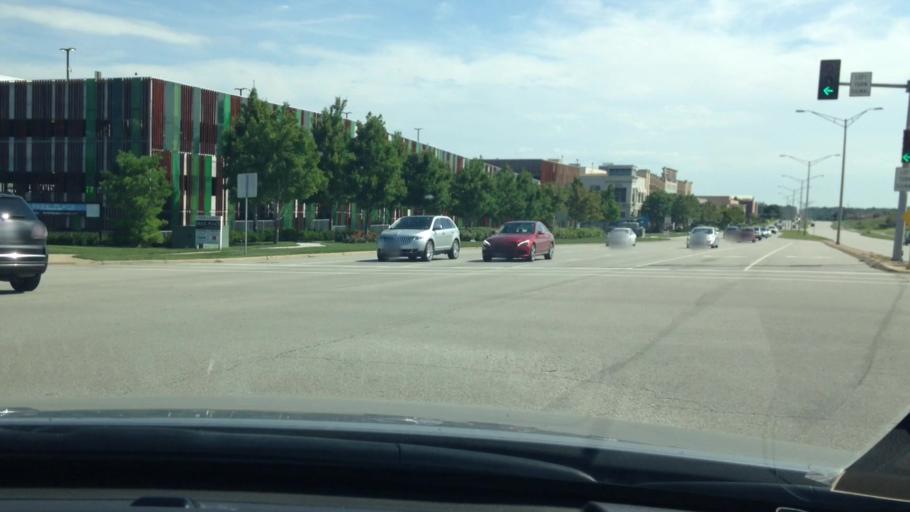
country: US
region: Kansas
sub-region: Johnson County
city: Leawood
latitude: 38.9205
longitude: -94.6491
